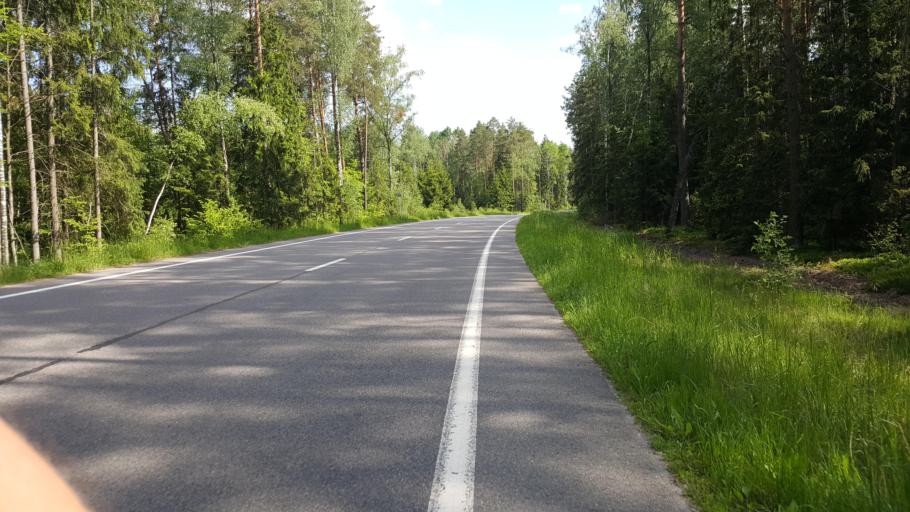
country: BY
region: Brest
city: Pruzhany
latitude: 52.5181
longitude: 24.1793
